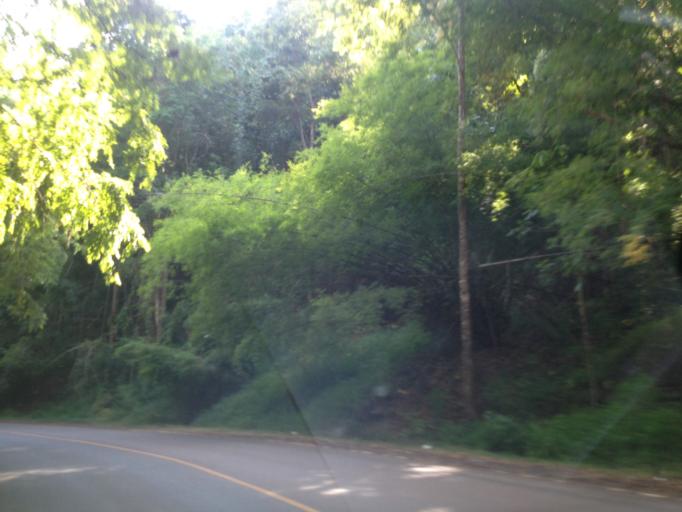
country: TH
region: Chiang Mai
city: Samoeng
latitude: 18.8236
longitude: 98.7852
